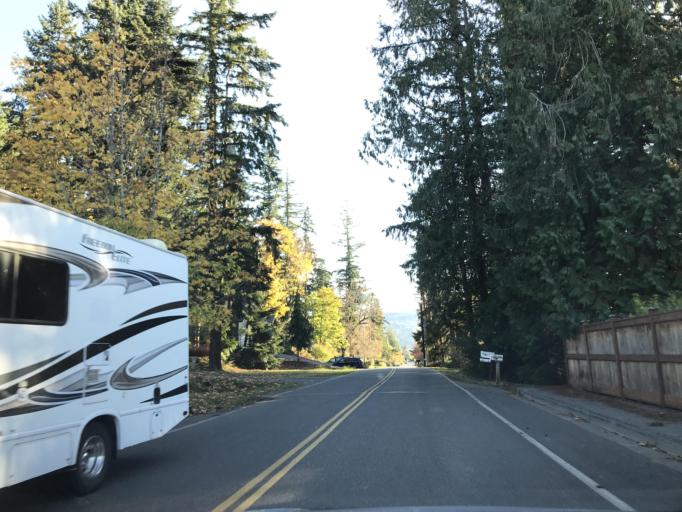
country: US
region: Washington
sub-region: Whatcom County
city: Geneva
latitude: 48.7736
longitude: -122.4031
